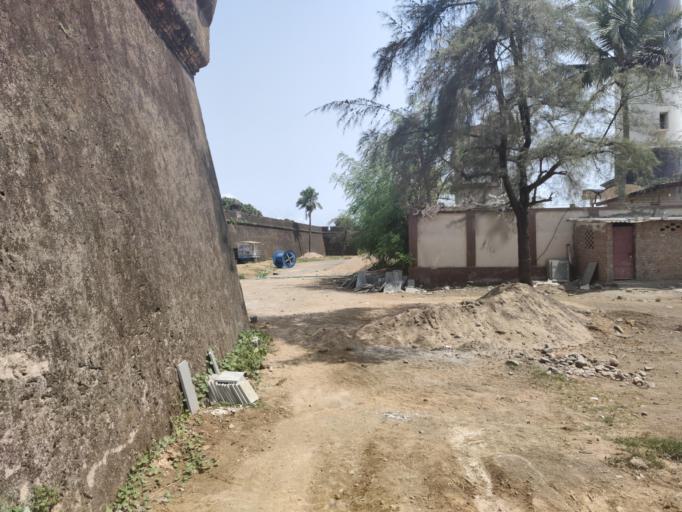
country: IN
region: Daman and Diu
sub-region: Daman District
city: Daman
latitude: 20.4099
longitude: 72.8311
